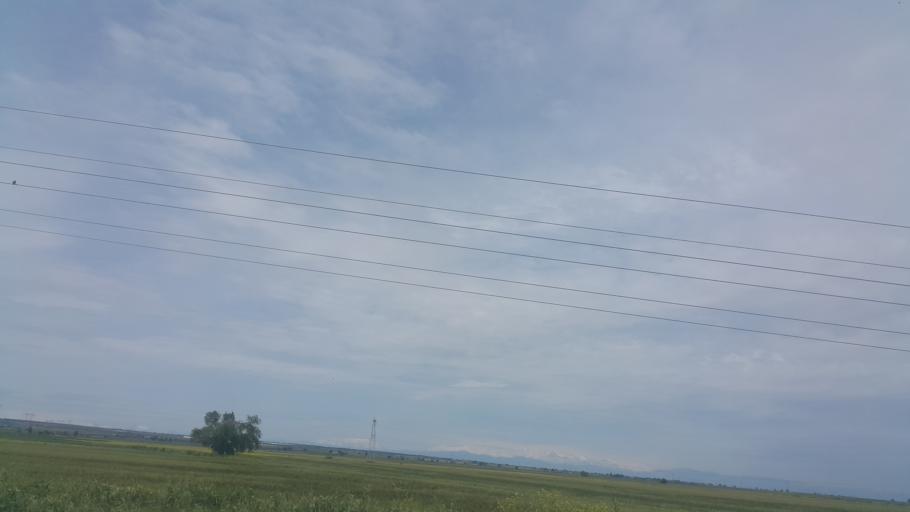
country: TR
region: Adana
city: Yakapinar
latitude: 37.0126
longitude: 35.7080
